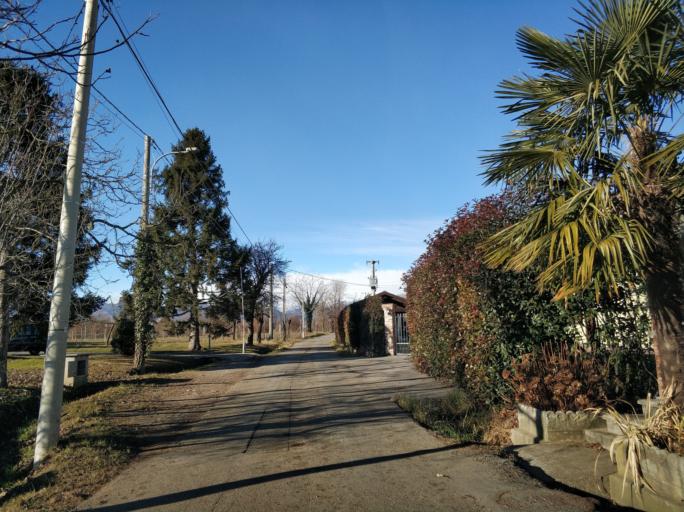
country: IT
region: Piedmont
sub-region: Provincia di Torino
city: Vauda Canavese Superiore
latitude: 45.2658
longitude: 7.6367
